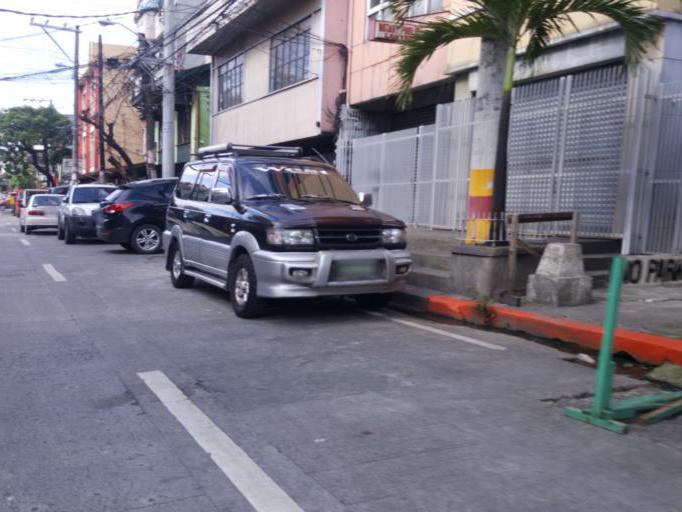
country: PH
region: Metro Manila
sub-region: City of Manila
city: Manila
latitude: 14.6187
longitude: 120.9818
